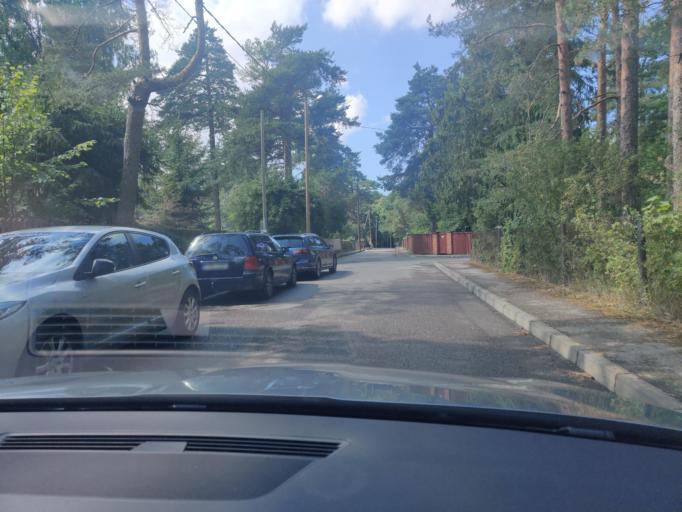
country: EE
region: Harju
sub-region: Saue vald
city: Laagri
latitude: 59.3708
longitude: 24.6255
